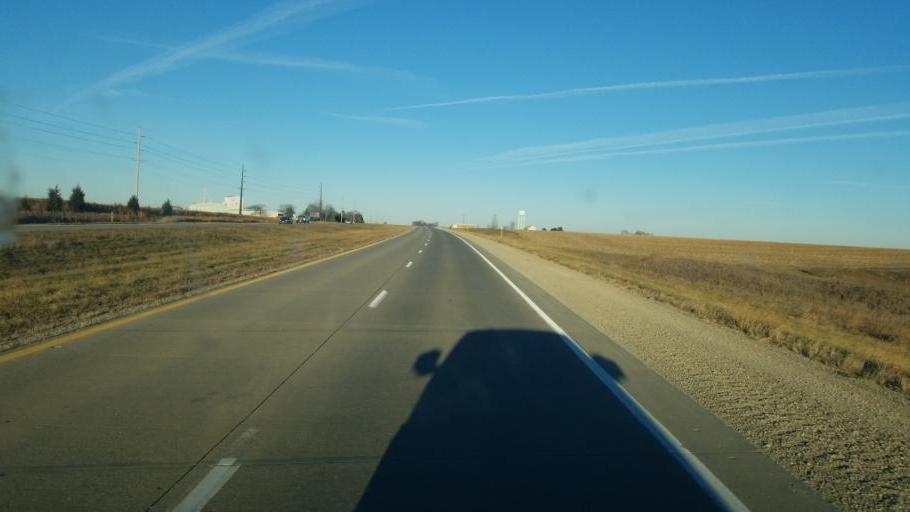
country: US
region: Iowa
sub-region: Mahaska County
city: Oskaloosa
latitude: 41.3257
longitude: -92.7078
